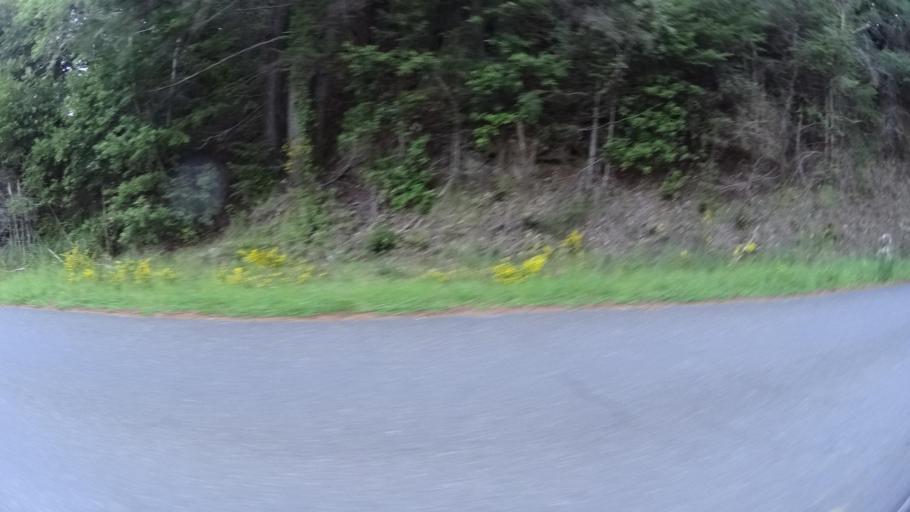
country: US
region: California
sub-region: Humboldt County
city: Bayside
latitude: 40.7590
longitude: -124.0232
